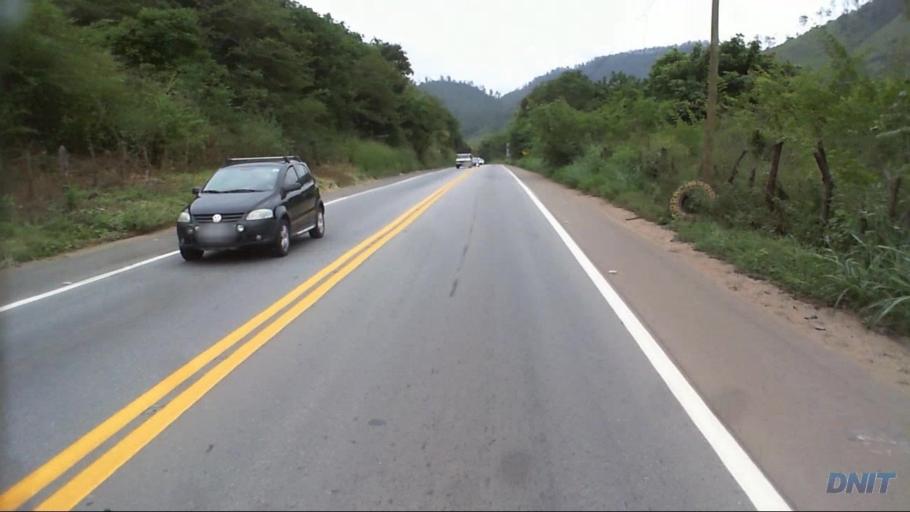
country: BR
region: Minas Gerais
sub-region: Timoteo
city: Timoteo
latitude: -19.5489
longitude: -42.6983
